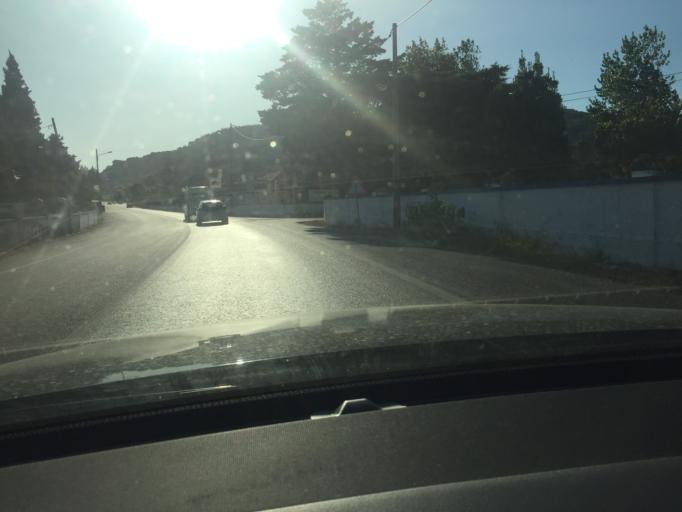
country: PT
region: Setubal
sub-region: Setubal
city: Setubal
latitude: 38.5326
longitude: -8.9118
